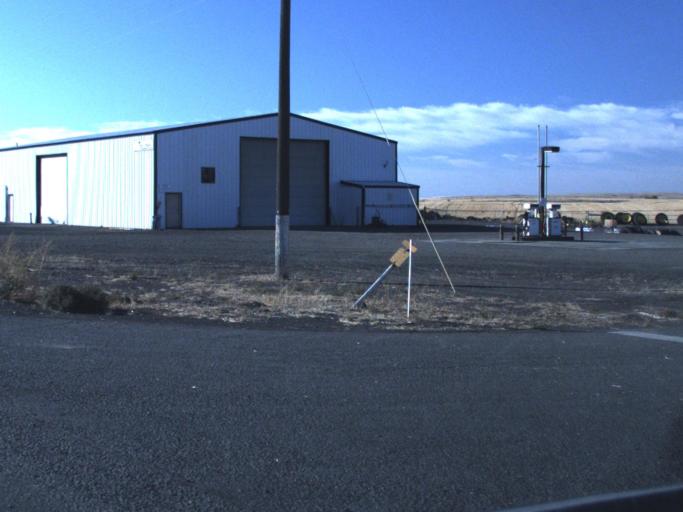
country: US
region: Washington
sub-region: Walla Walla County
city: Garrett
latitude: 46.2965
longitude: -118.6384
